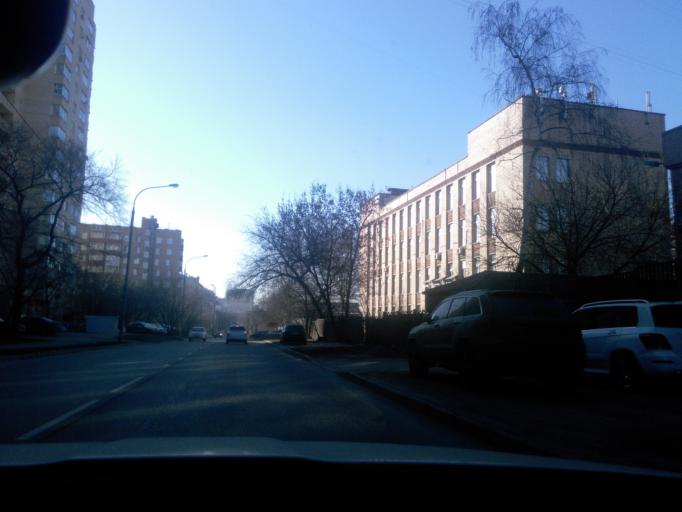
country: RU
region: Moscow
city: Sokol
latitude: 55.7964
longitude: 37.5034
